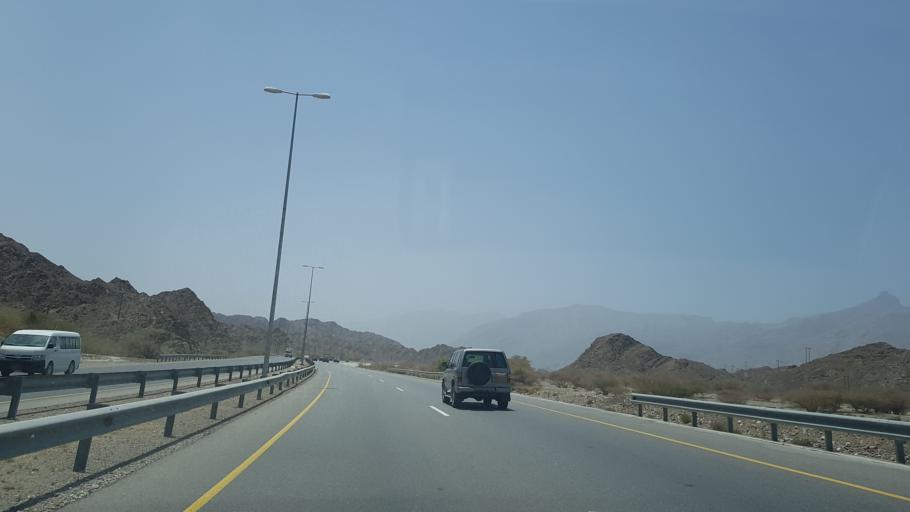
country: OM
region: Muhafazat ad Dakhiliyah
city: Sufalat Sama'il
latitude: 23.3428
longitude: 57.9993
